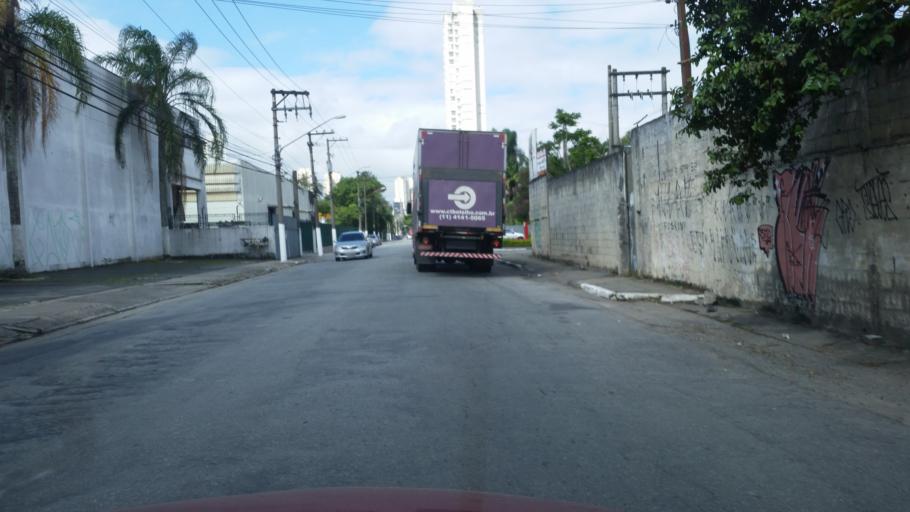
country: BR
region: Sao Paulo
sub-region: Diadema
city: Diadema
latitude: -23.6719
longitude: -46.6993
